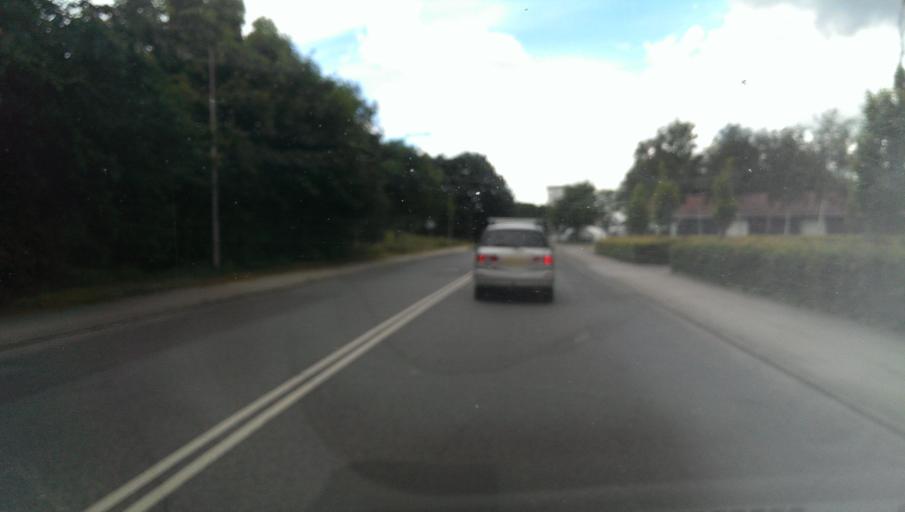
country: DK
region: South Denmark
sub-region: Esbjerg Kommune
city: Esbjerg
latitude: 55.4770
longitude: 8.4946
